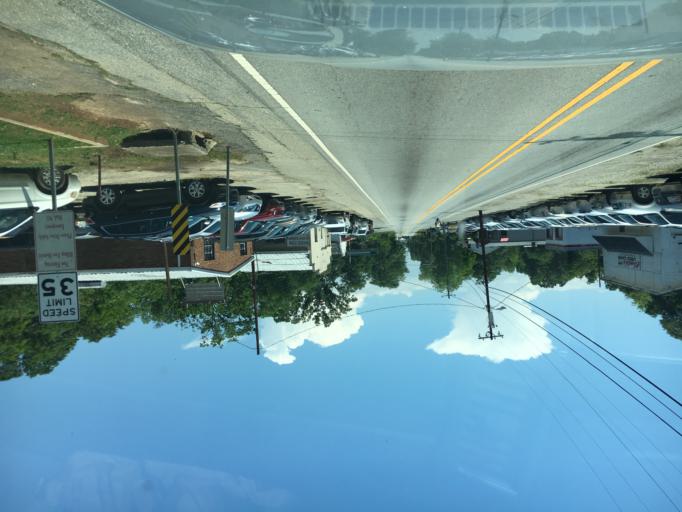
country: US
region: South Carolina
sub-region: Spartanburg County
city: Saxon
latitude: 34.9636
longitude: -81.9536
